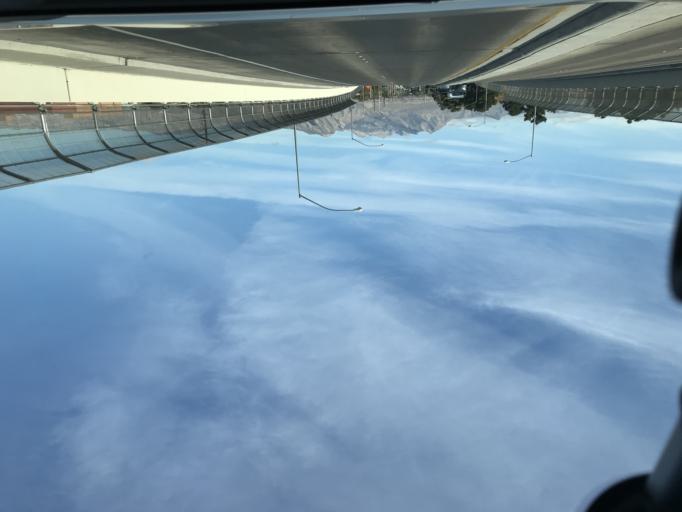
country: US
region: Nevada
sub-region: Clark County
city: Spring Valley
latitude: 36.2034
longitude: -115.2441
